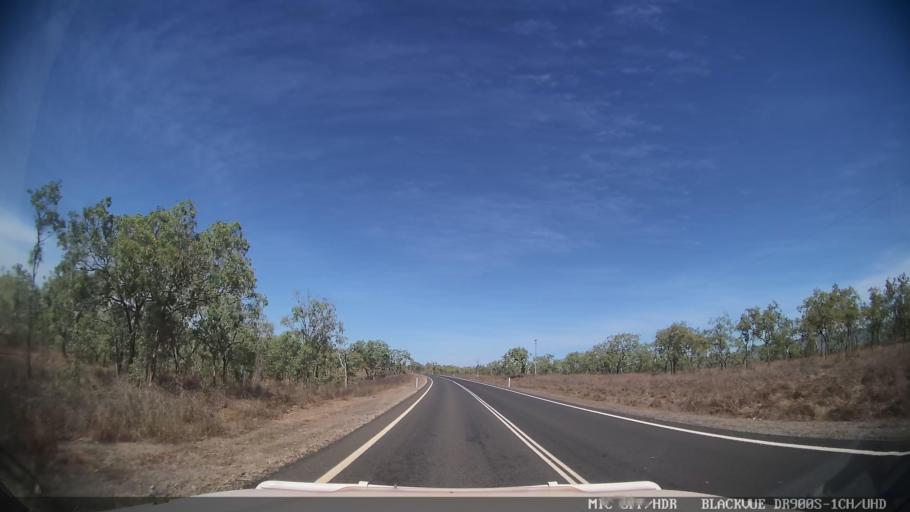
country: AU
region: Queensland
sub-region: Cook
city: Cooktown
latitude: -15.7882
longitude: 144.7034
